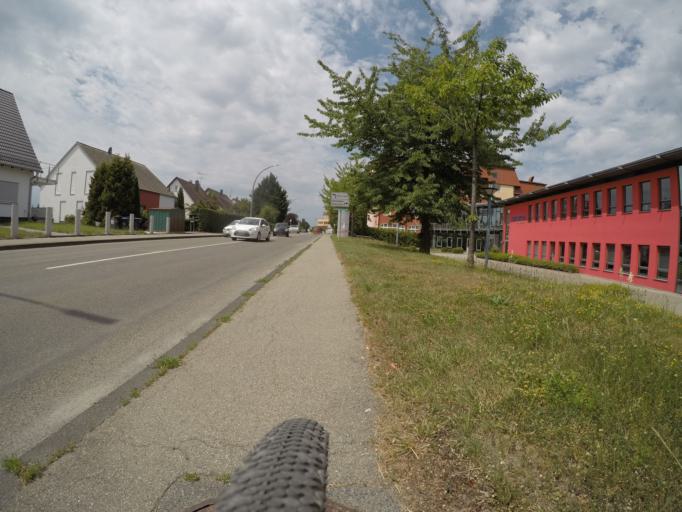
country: DE
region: Baden-Wuerttemberg
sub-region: Regierungsbezirk Stuttgart
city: Magstadt
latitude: 48.7267
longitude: 8.9748
